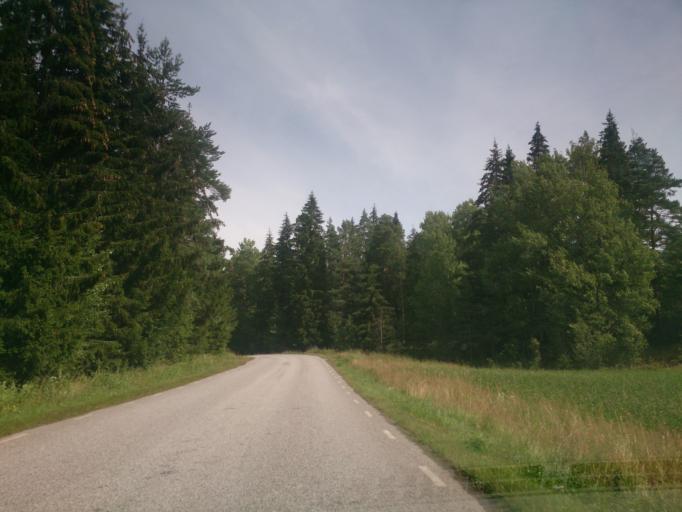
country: SE
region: OEstergoetland
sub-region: Valdemarsviks Kommun
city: Gusum
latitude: 58.3292
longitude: 16.5830
